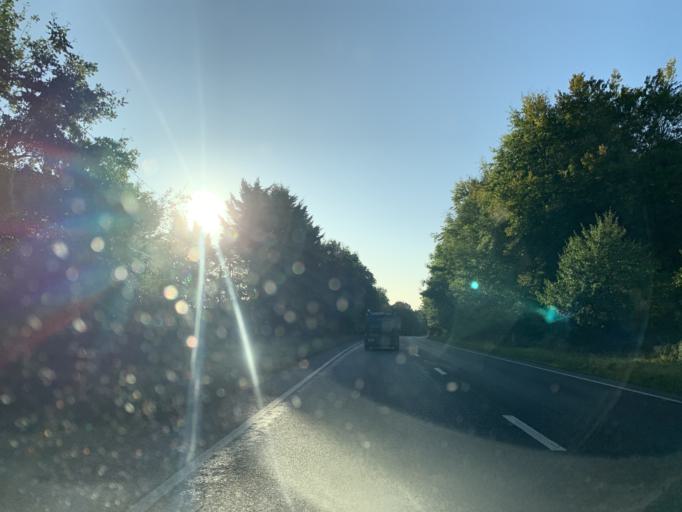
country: GB
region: England
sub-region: Wiltshire
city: Whiteparish
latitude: 51.0054
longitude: -1.6684
